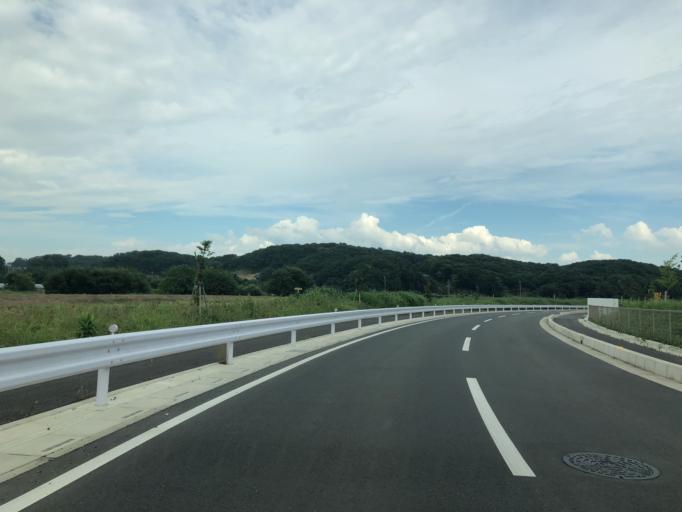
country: JP
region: Saitama
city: Fukiage-fujimi
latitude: 36.0451
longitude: 139.4154
